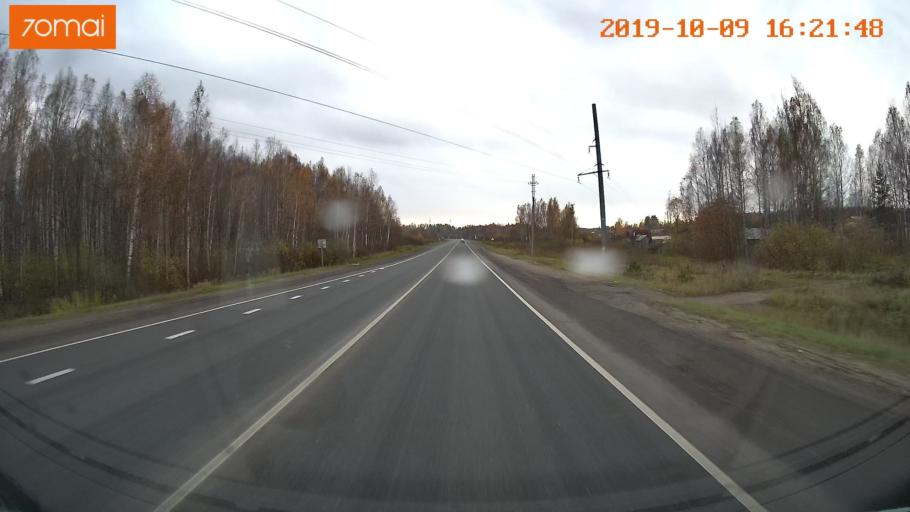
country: RU
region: Kostroma
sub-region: Kostromskoy Rayon
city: Kostroma
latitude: 57.6863
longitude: 40.8880
